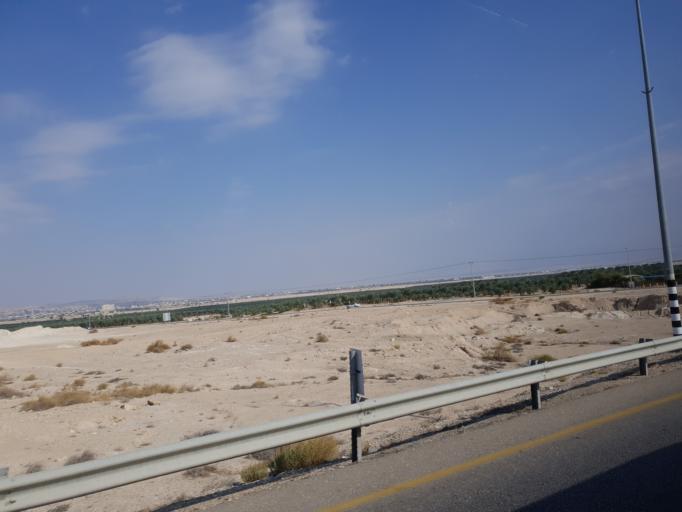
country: PS
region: West Bank
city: Jericho
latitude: 31.8015
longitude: 35.4484
